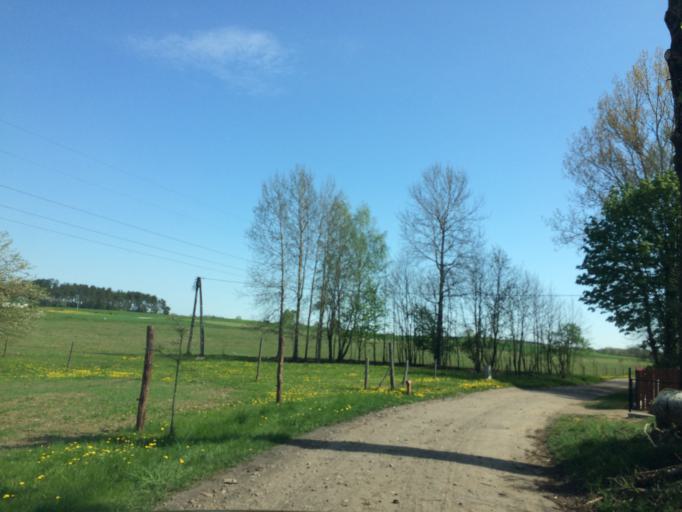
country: PL
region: Warmian-Masurian Voivodeship
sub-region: Powiat dzialdowski
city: Rybno
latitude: 53.4214
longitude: 19.9121
